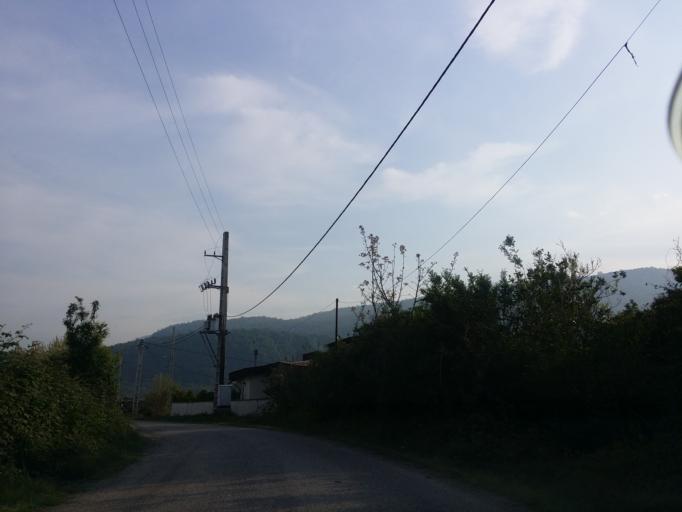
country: IR
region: Mazandaran
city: Chalus
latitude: 36.6642
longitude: 51.3651
